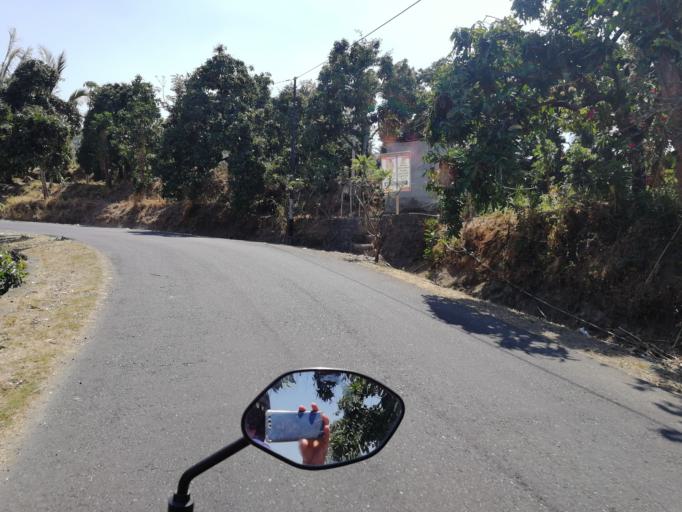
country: ID
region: Bali
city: Banjar Kedisan
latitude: -8.1365
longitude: 115.3225
